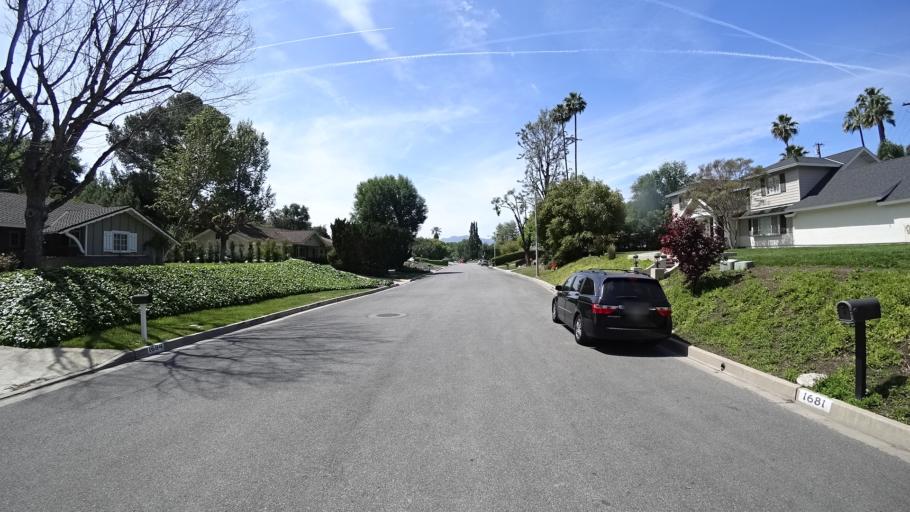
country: US
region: California
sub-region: Ventura County
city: Thousand Oaks
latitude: 34.2056
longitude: -118.8481
